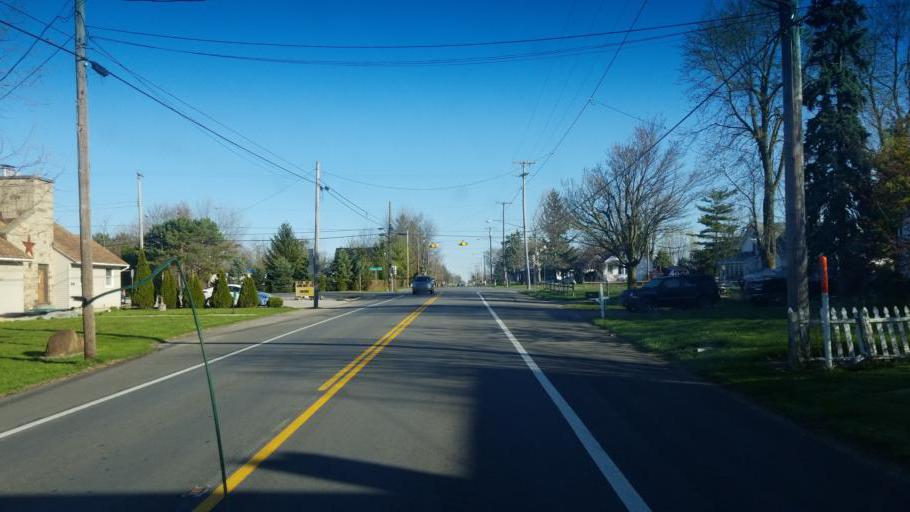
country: US
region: Ohio
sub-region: Union County
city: Richwood
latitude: 40.4531
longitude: -83.4549
